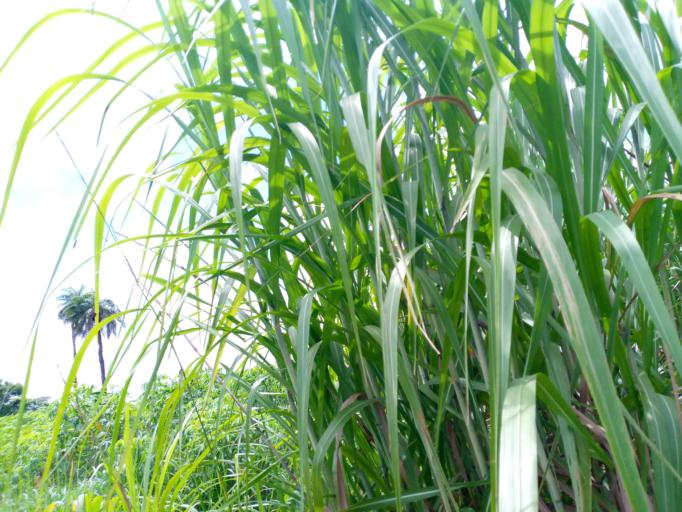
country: SL
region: Northern Province
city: Magburaka
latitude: 8.7158
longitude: -11.9249
